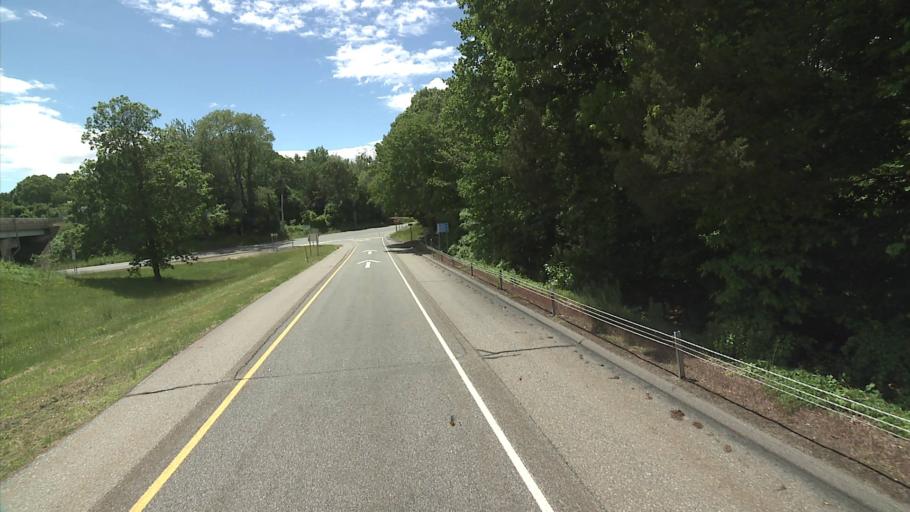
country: US
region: Connecticut
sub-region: Middlesex County
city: Saybrook Manor
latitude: 41.2994
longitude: -72.3925
